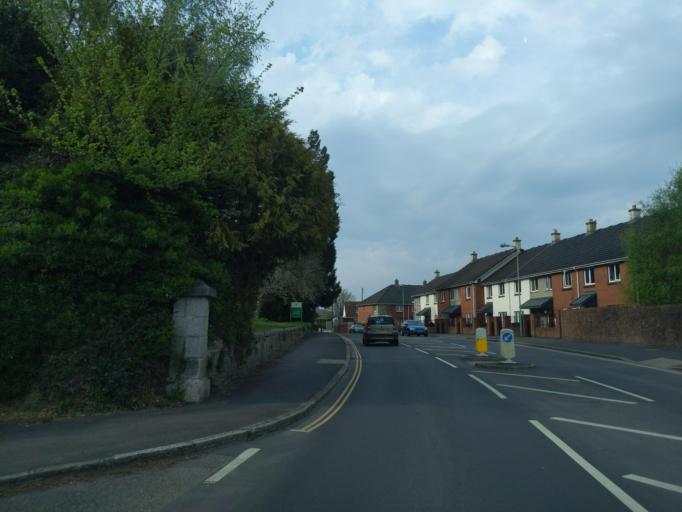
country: GB
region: England
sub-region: Devon
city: Exeter
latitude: 50.7228
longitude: -3.5488
